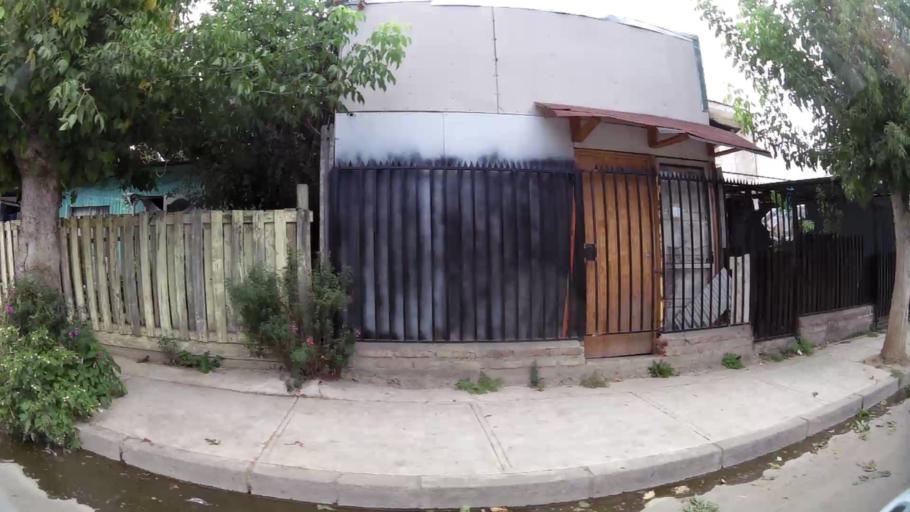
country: CL
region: O'Higgins
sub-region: Provincia de Cachapoal
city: Graneros
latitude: -34.0769
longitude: -70.7331
